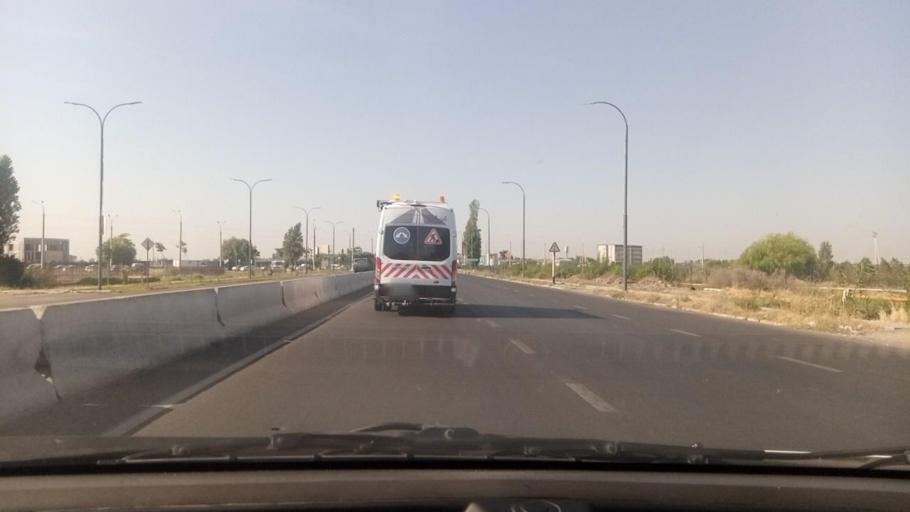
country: UZ
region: Toshkent Shahri
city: Bektemir
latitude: 41.2043
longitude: 69.3327
